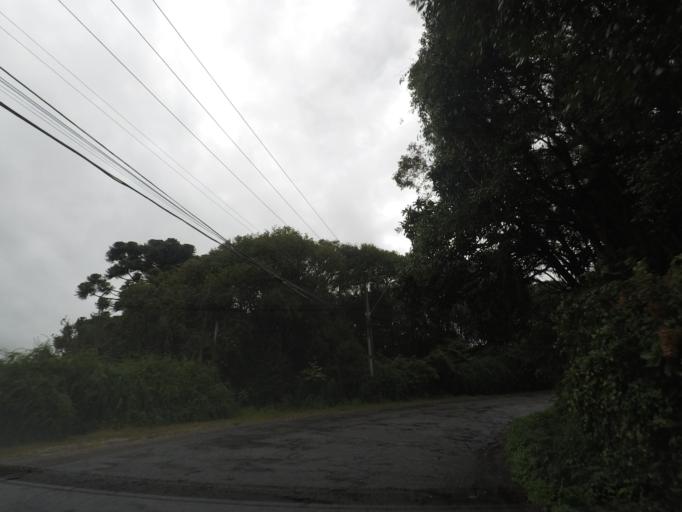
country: BR
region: Parana
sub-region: Campo Largo
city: Campo Largo
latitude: -25.4527
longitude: -49.4487
